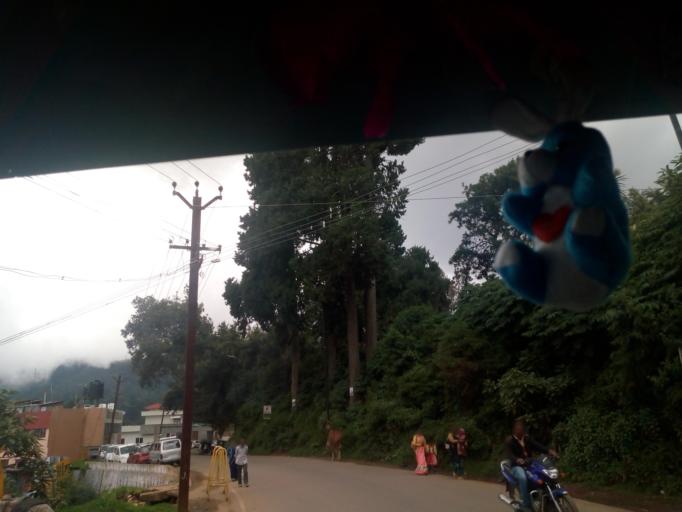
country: IN
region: Tamil Nadu
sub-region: Nilgiri
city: Ooty
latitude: 11.4081
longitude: 76.7073
